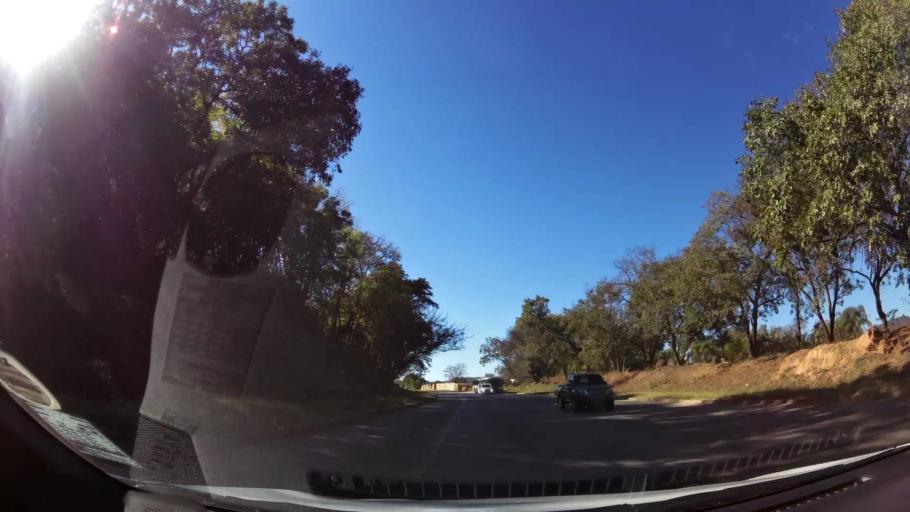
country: ZA
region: Limpopo
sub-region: Mopani District Municipality
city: Tzaneen
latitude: -23.8370
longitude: 30.1817
